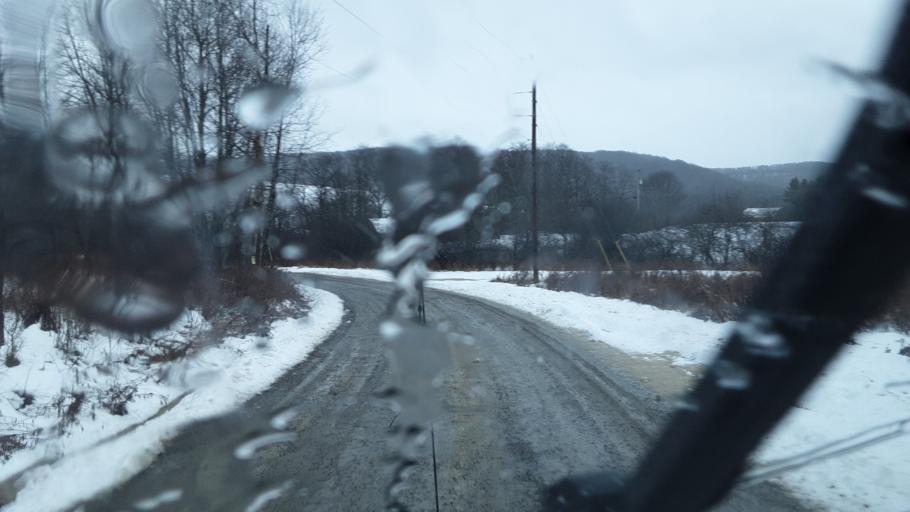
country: US
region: Pennsylvania
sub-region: Tioga County
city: Westfield
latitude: 41.9603
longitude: -77.7099
